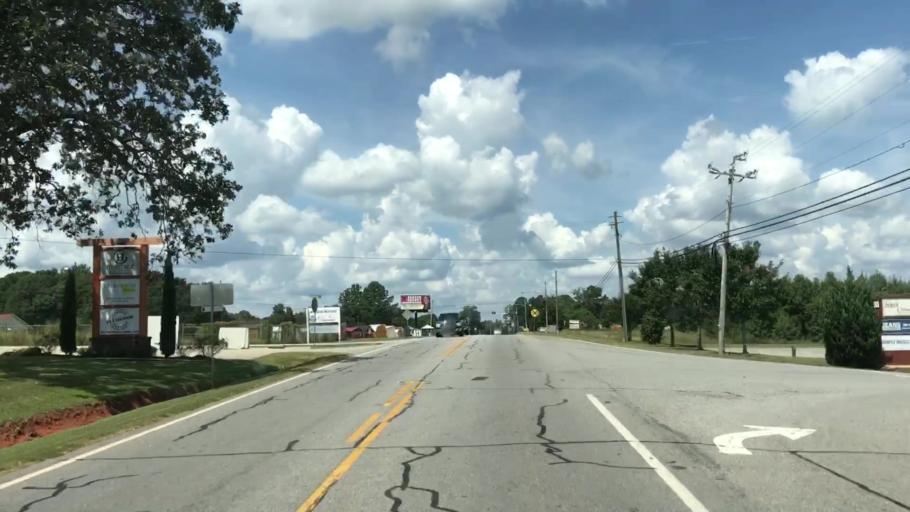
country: US
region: Georgia
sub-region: Oconee County
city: Watkinsville
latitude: 33.8562
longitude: -83.4022
